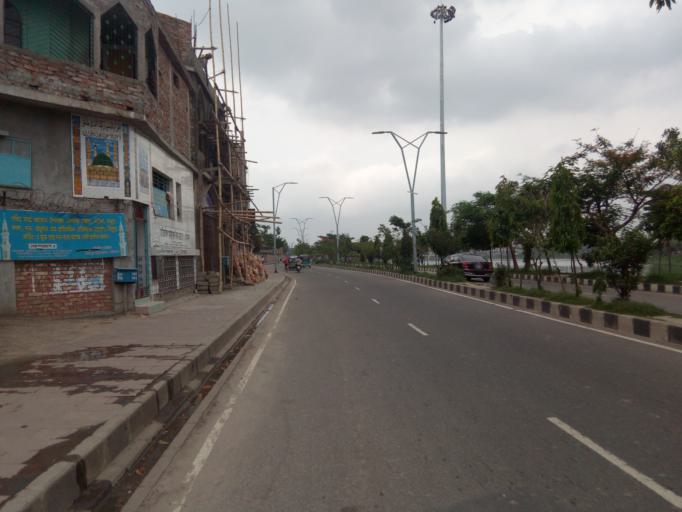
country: BD
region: Dhaka
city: Paltan
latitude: 23.7589
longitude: 90.4044
